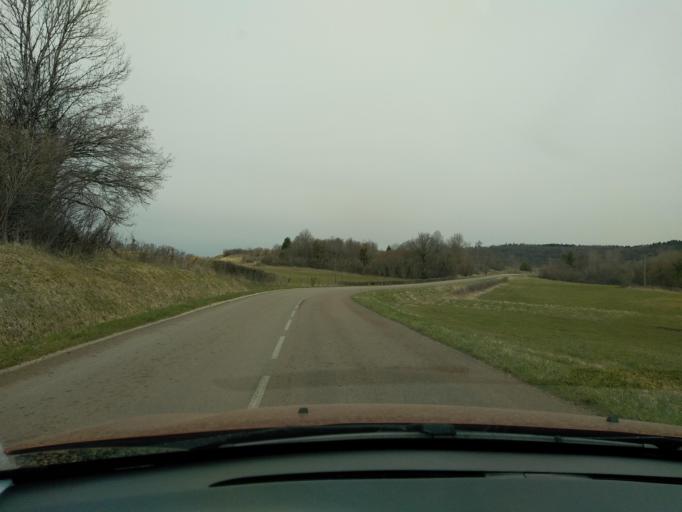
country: FR
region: Franche-Comte
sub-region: Departement du Jura
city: Clairvaux-les-Lacs
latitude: 46.6168
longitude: 5.7394
